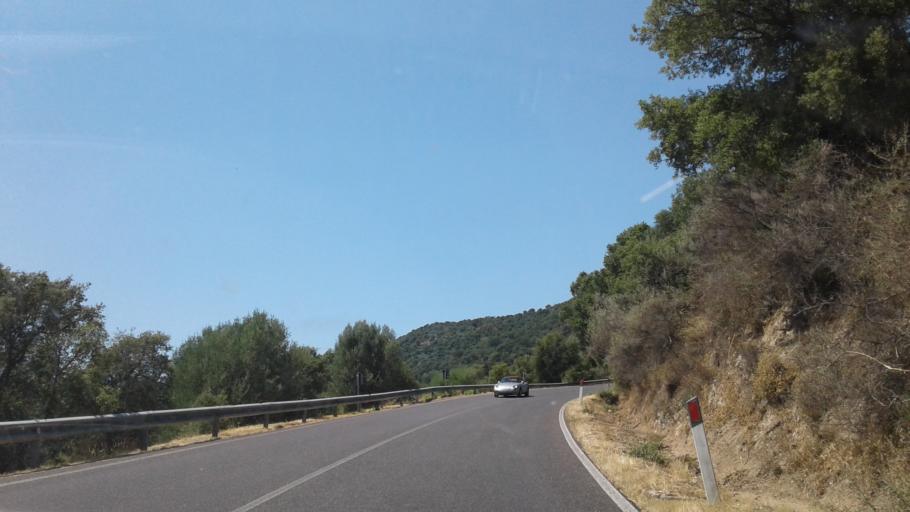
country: IT
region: Sardinia
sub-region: Provincia di Olbia-Tempio
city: Luras
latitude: 40.9463
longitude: 9.1981
